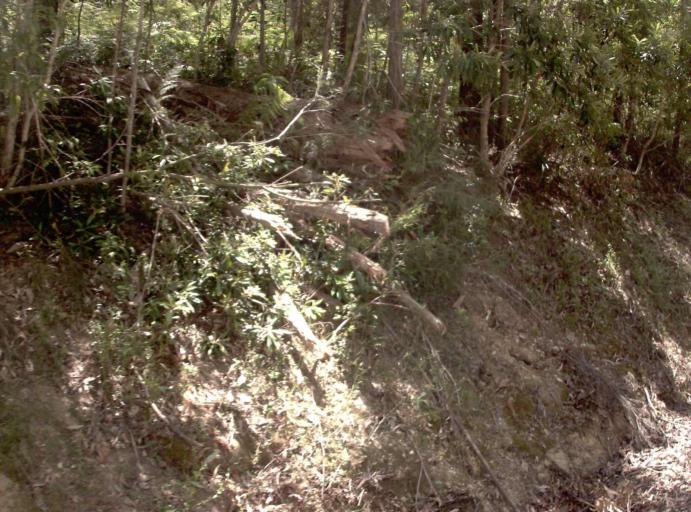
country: AU
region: New South Wales
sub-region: Bombala
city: Bombala
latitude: -37.4920
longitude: 148.9255
